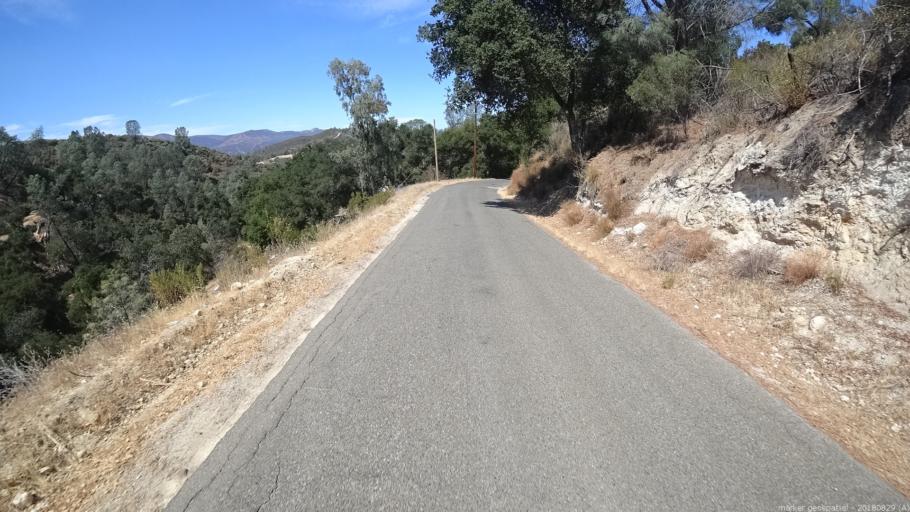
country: US
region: California
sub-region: San Luis Obispo County
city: Lake Nacimiento
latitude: 35.8218
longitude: -121.0666
